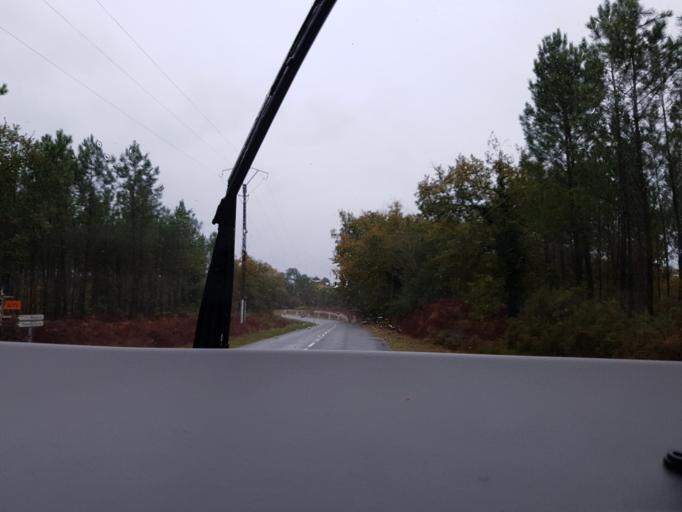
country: FR
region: Aquitaine
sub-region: Departement des Landes
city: Pissos
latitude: 44.3717
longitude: -0.6468
